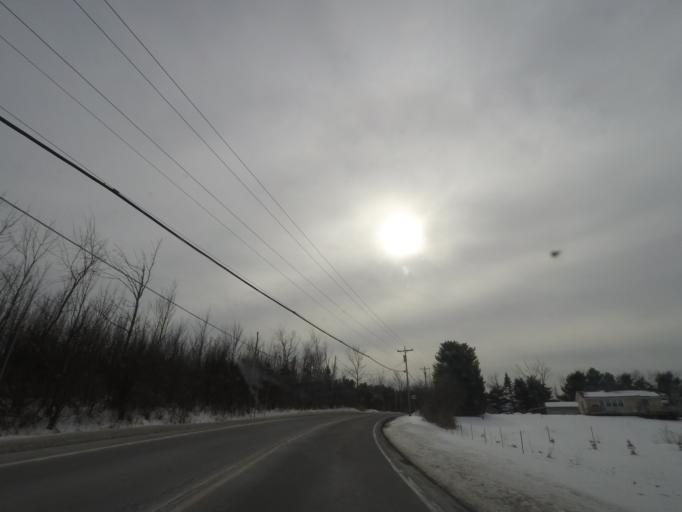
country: US
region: New York
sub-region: Albany County
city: Altamont
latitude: 42.6952
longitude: -74.0564
